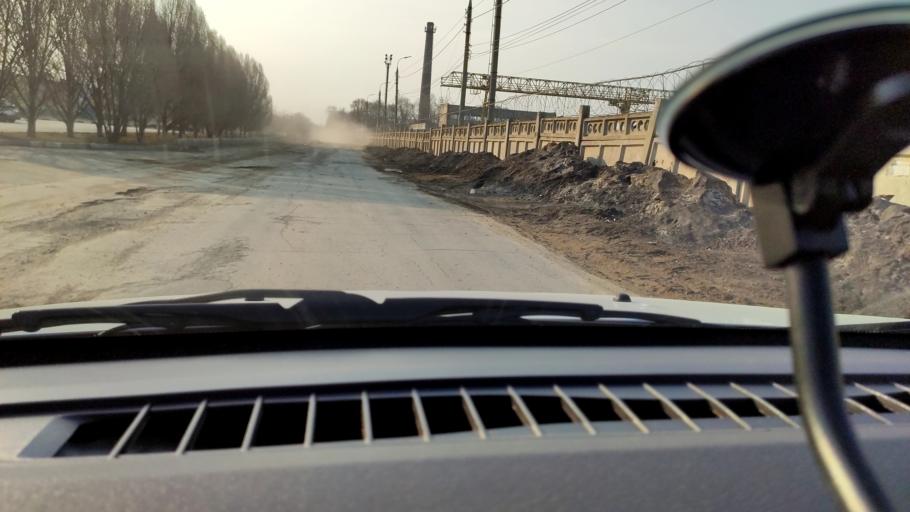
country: RU
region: Samara
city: Samara
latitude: 53.1842
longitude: 50.2612
